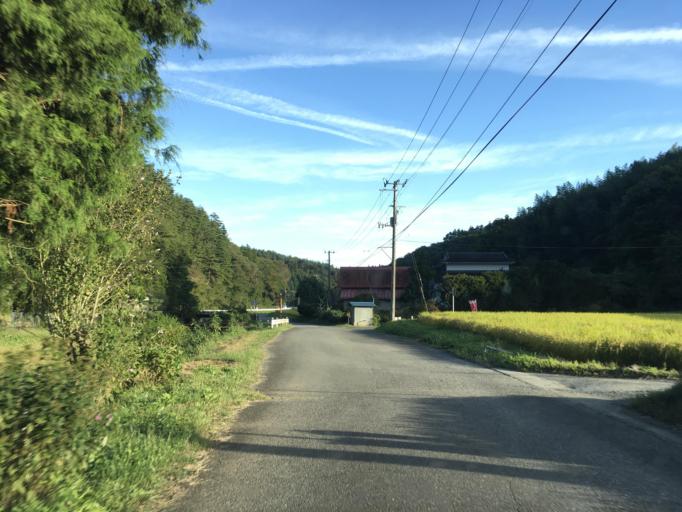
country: JP
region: Iwate
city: Ichinoseki
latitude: 38.7929
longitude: 141.4213
